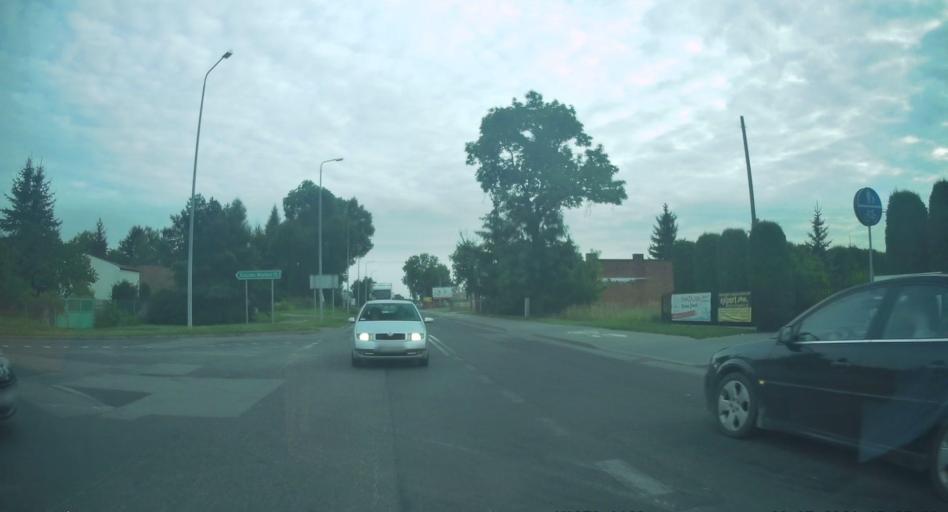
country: PL
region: Lodz Voivodeship
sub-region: Powiat radomszczanski
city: Radomsko
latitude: 51.0538
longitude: 19.4401
